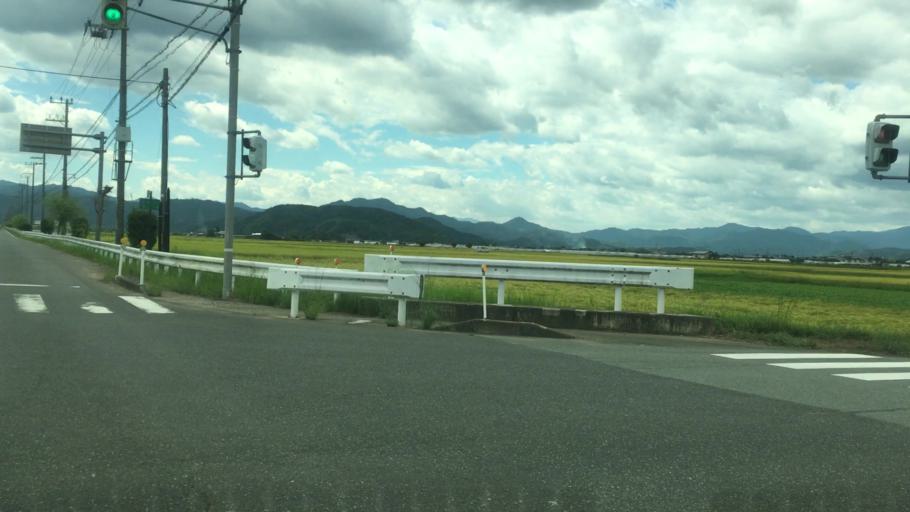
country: JP
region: Hyogo
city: Toyooka
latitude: 35.5247
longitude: 134.8398
